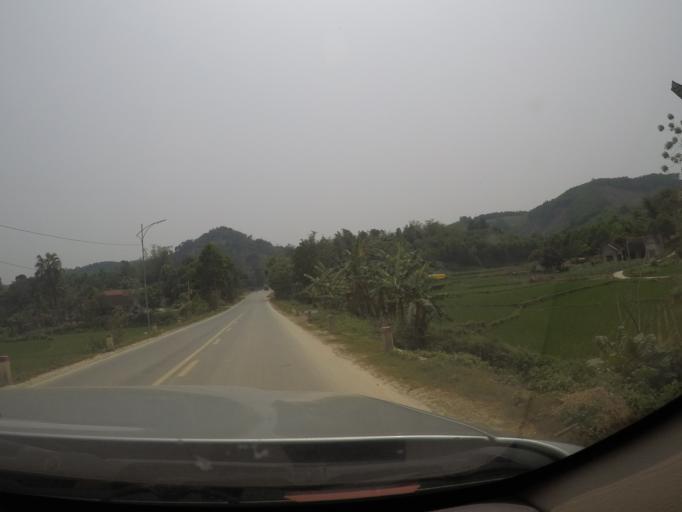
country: VN
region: Thanh Hoa
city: Thi Tran Yen Cat
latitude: 19.6797
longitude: 105.4554
